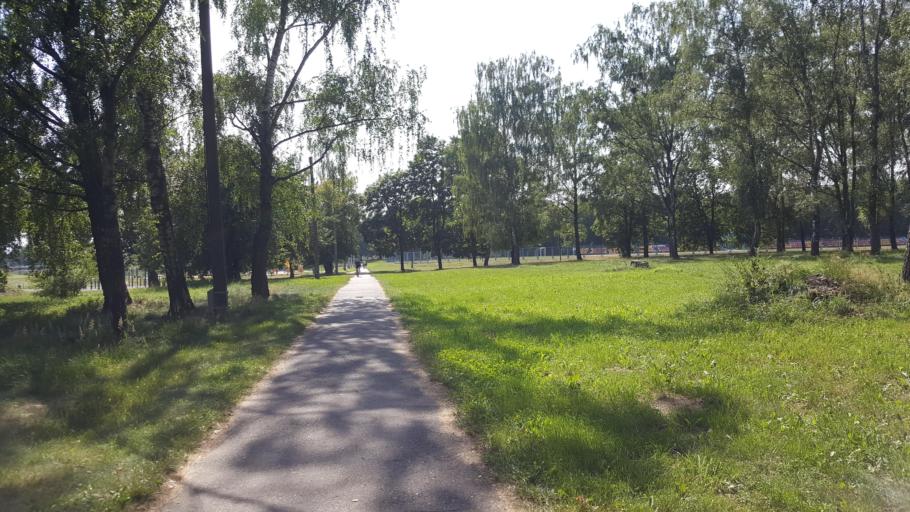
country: BY
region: Brest
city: Zhabinka
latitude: 52.1946
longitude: 24.0284
